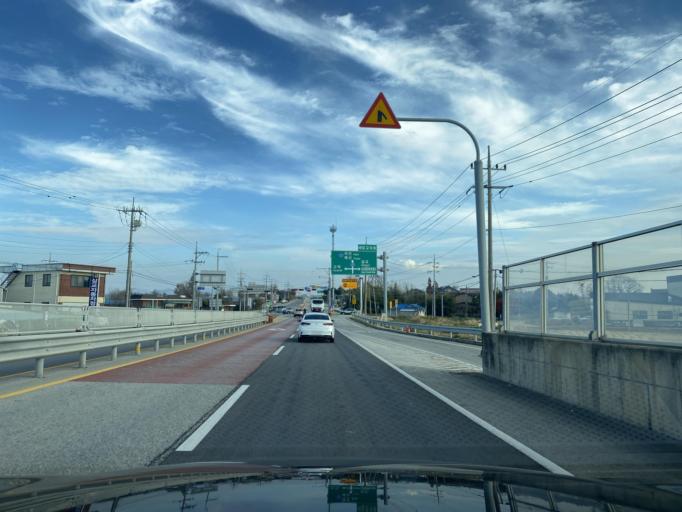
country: KR
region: Chungcheongnam-do
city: Yesan
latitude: 36.6908
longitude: 126.7415
